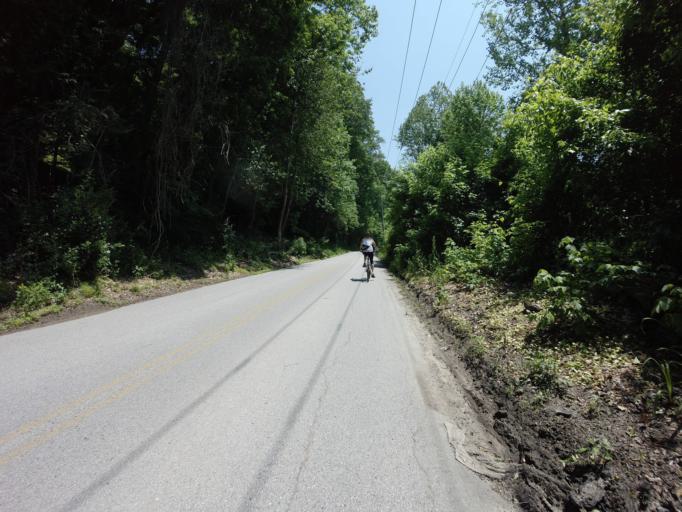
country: US
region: Maryland
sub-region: Howard County
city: Ilchester
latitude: 39.2570
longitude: -76.7759
